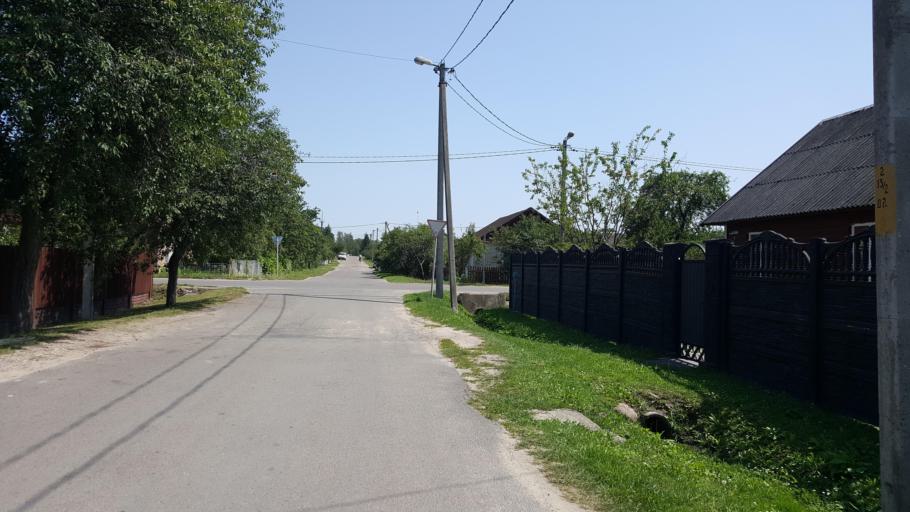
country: BY
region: Brest
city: Zhabinka
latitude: 52.1943
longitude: 24.0127
